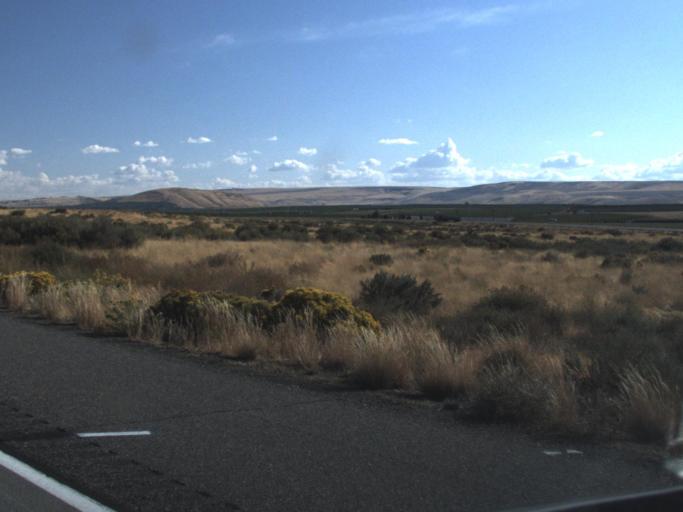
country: US
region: Washington
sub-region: Benton County
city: West Richland
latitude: 46.2502
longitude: -119.3702
